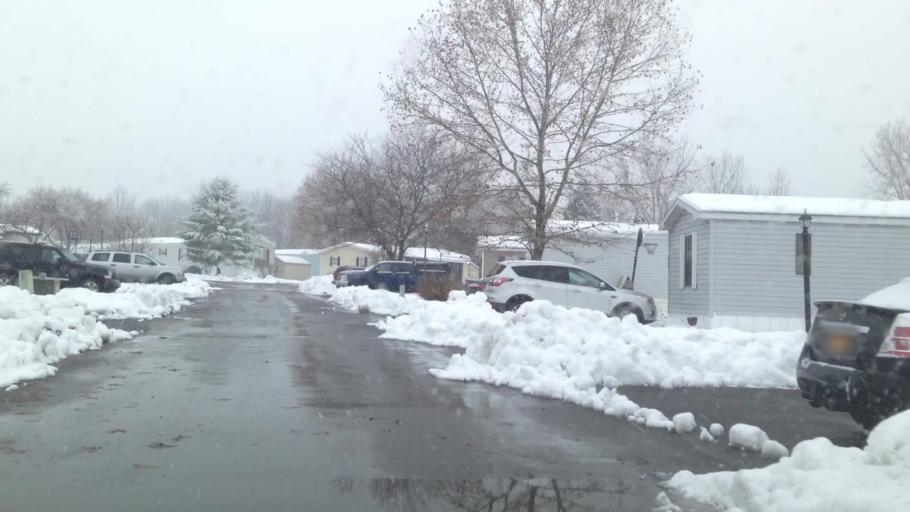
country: US
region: New York
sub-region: Onondaga County
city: Elbridge
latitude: 43.0420
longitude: -76.4138
